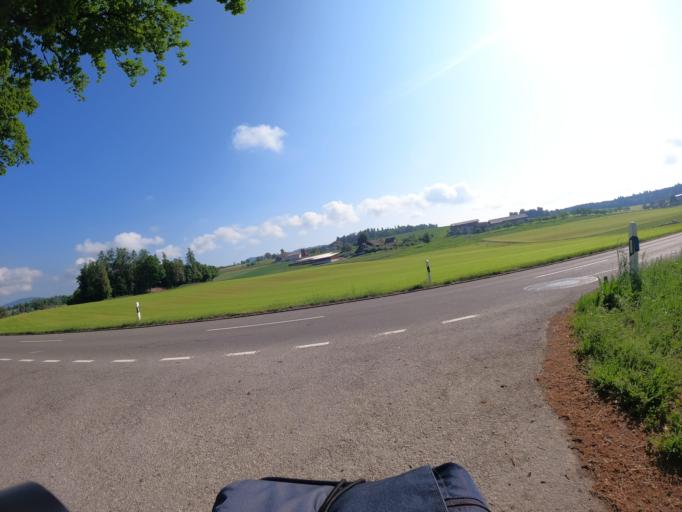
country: CH
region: Zug
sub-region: Zug
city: Steinhausen
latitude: 47.2157
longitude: 8.5034
